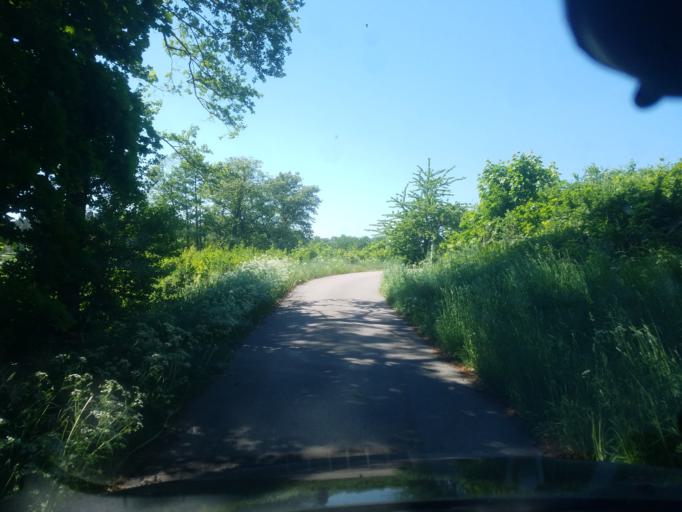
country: SE
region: Vaestra Goetaland
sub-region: Orust
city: Henan
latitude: 58.2624
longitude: 11.5724
